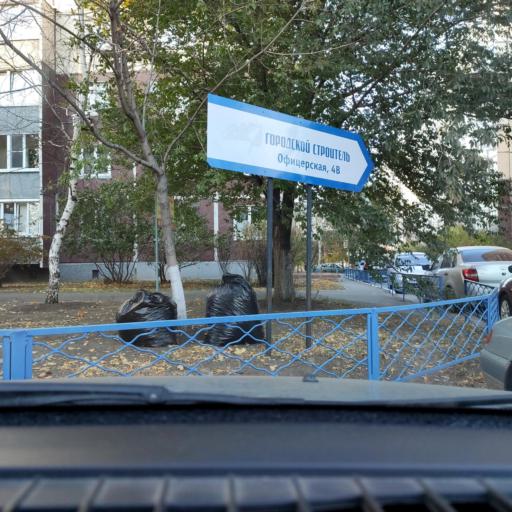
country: RU
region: Samara
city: Tol'yatti
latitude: 53.5457
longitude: 49.3214
